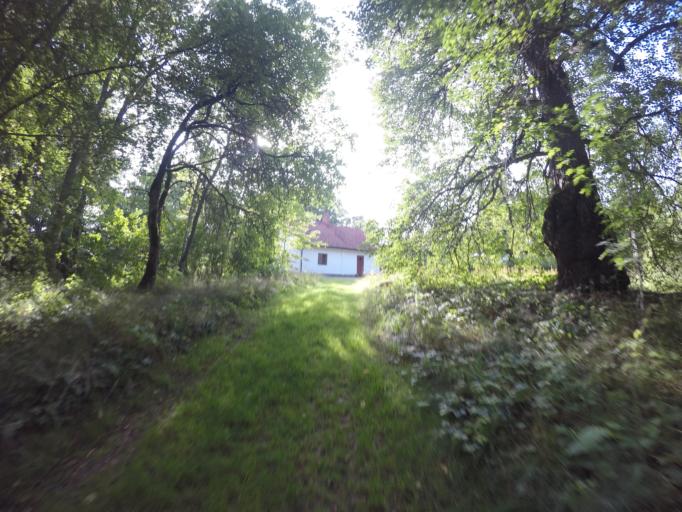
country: SE
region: Soedermanland
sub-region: Eskilstuna Kommun
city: Kvicksund
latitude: 59.4806
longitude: 16.2897
